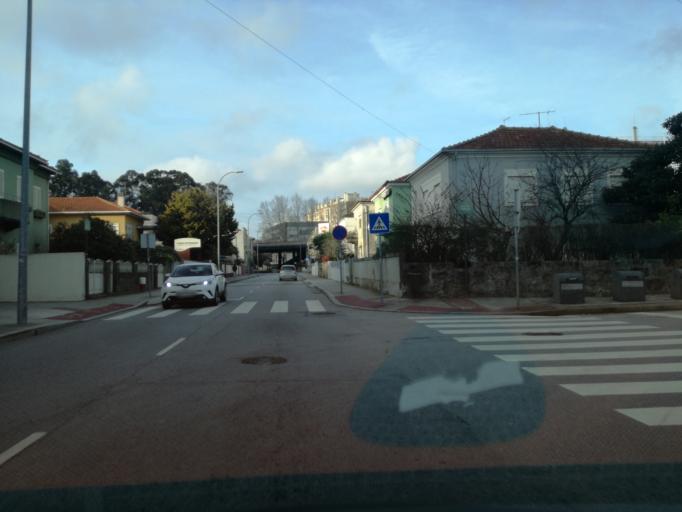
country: PT
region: Porto
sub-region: Porto
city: Porto
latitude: 41.1716
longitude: -8.6260
